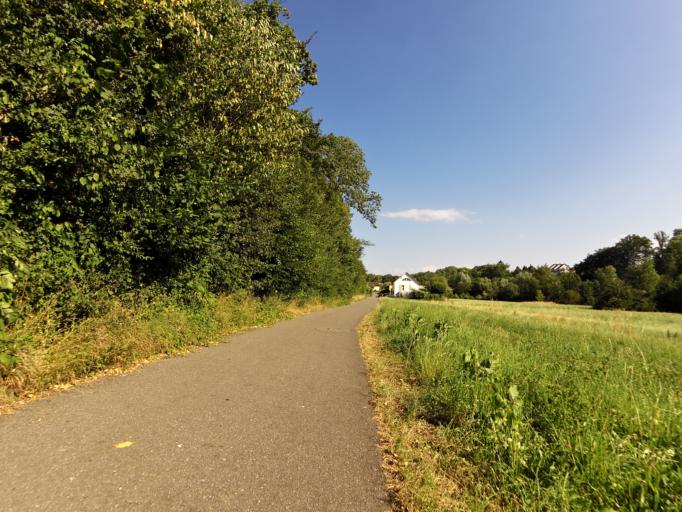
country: CH
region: Aargau
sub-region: Bezirk Lenzburg
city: Niederlenz
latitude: 47.4159
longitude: 8.1771
